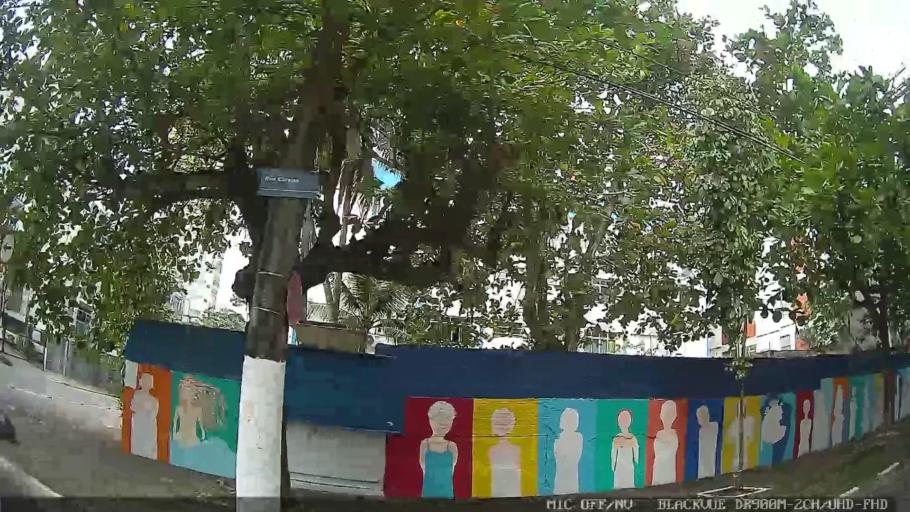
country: BR
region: Sao Paulo
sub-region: Guaruja
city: Guaruja
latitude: -24.0120
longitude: -46.2719
